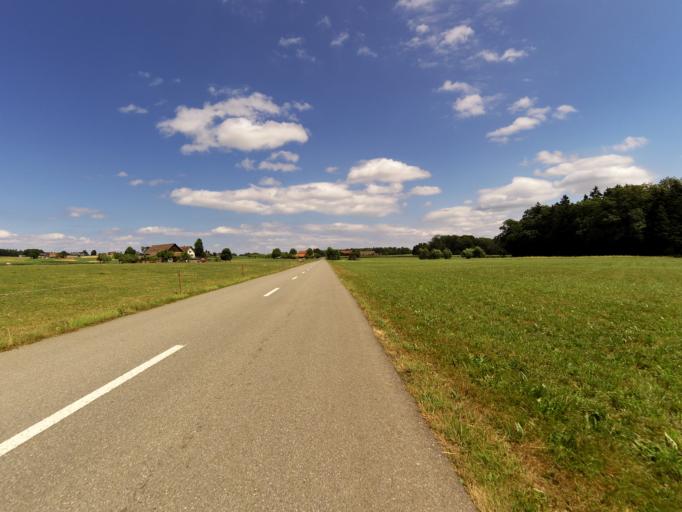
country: CH
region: Thurgau
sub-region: Weinfelden District
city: Maerstetten-Dorf
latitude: 47.6245
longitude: 9.0911
